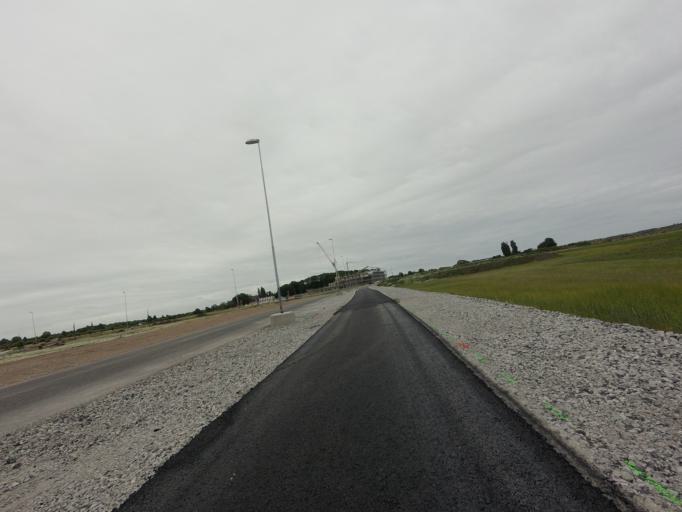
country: SE
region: Skane
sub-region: Malmo
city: Bunkeflostrand
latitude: 55.5672
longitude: 12.9452
